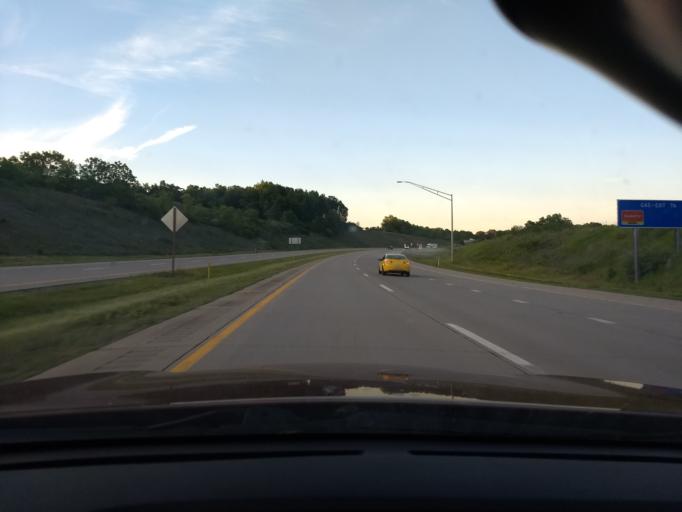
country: US
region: Pennsylvania
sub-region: Centre County
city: Houserville
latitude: 40.8401
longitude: -77.8309
